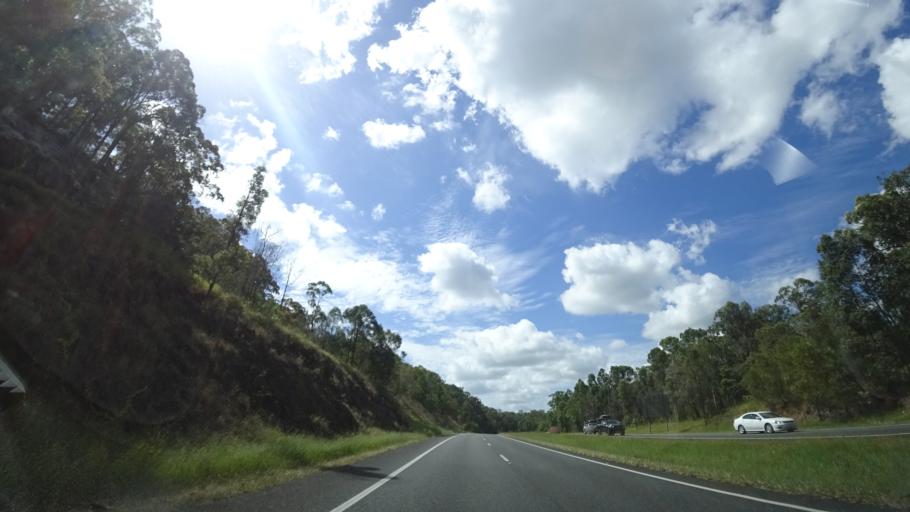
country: AU
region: Queensland
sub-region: Sunshine Coast
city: Nambour
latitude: -26.6091
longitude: 152.9751
